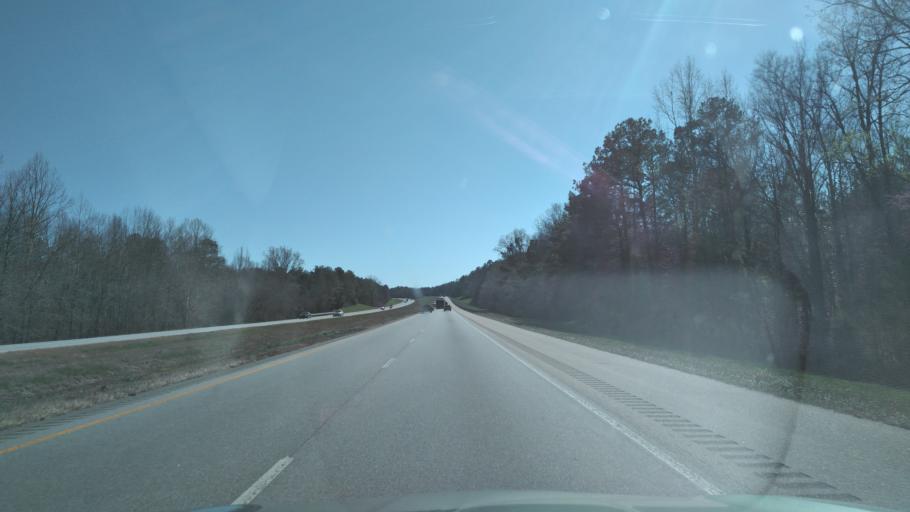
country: US
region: Alabama
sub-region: Lowndes County
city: Fort Deposit
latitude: 32.0154
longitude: -86.5190
